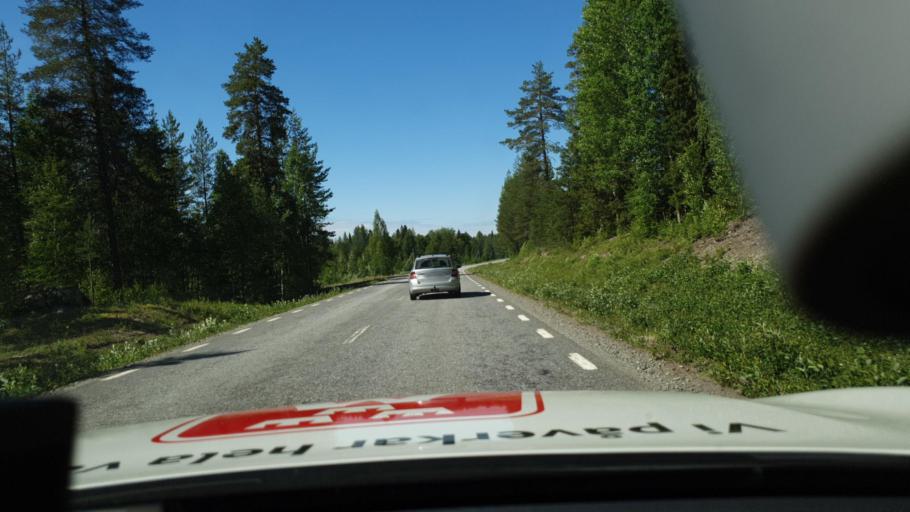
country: SE
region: Norrbotten
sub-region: Bodens Kommun
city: Saevast
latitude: 65.8782
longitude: 21.8677
